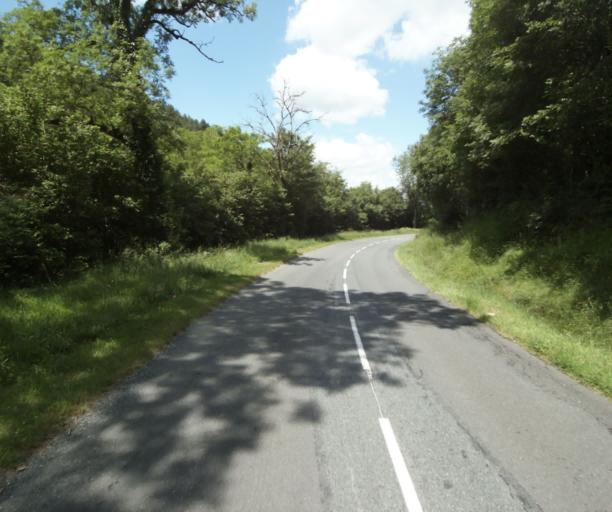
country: FR
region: Midi-Pyrenees
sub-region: Departement du Tarn
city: Soreze
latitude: 43.4195
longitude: 2.0604
